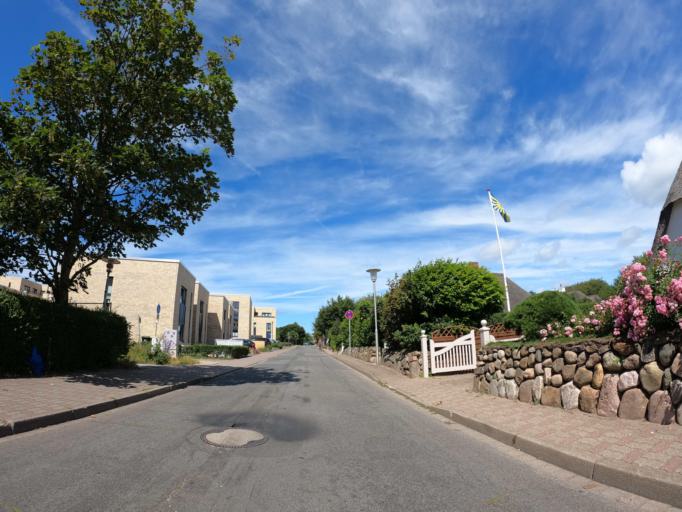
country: DE
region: Schleswig-Holstein
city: Westerland
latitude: 54.9108
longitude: 8.3171
